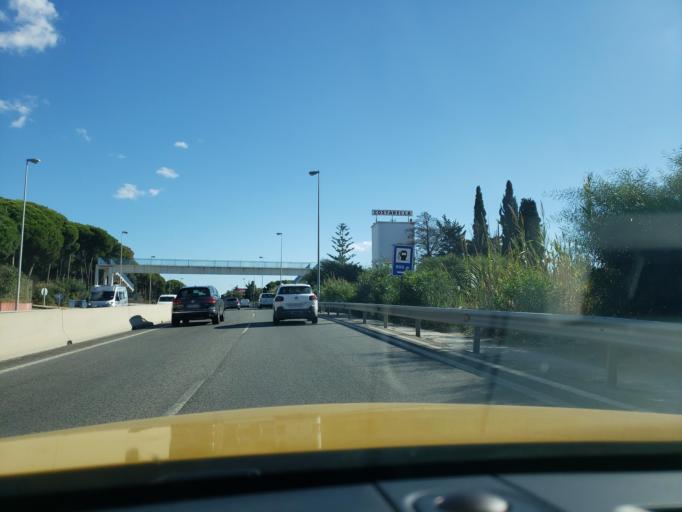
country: ES
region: Andalusia
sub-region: Provincia de Malaga
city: Ojen
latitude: 36.5021
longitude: -4.8055
